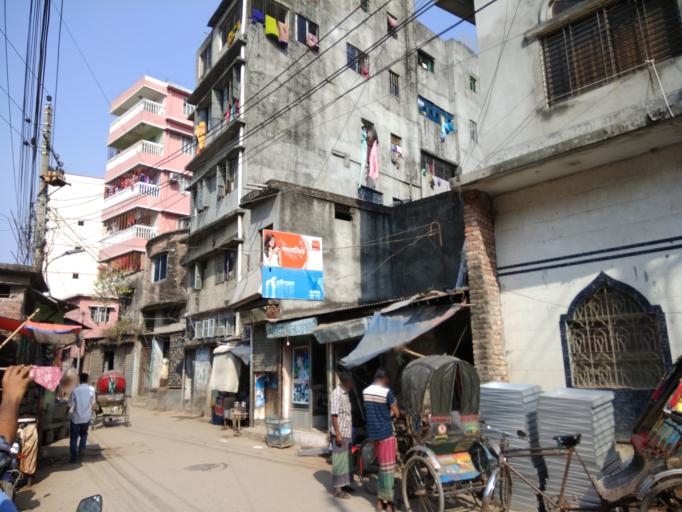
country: BD
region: Dhaka
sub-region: Dhaka
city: Dhaka
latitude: 23.7202
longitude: 90.4007
